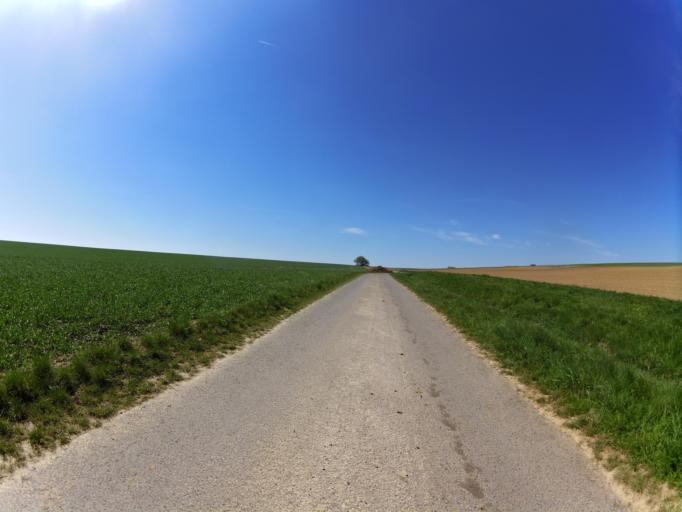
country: DE
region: Bavaria
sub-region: Regierungsbezirk Unterfranken
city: Winterhausen
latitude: 49.6897
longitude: 9.9906
